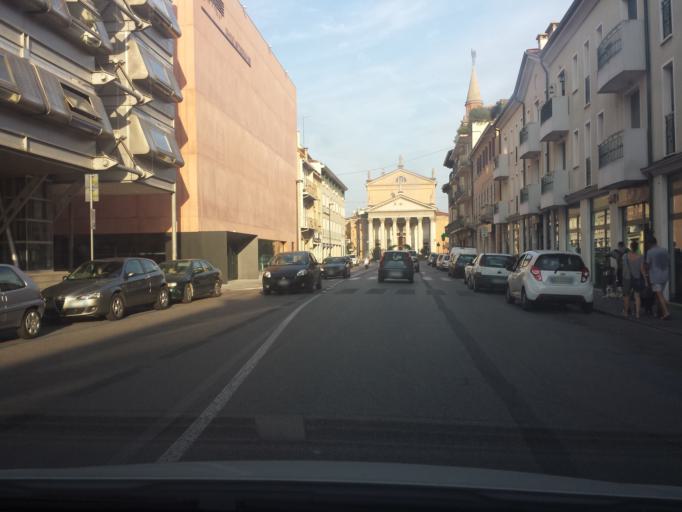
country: IT
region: Veneto
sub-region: Provincia di Venezia
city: San Dona di Piave
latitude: 45.6307
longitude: 12.5640
